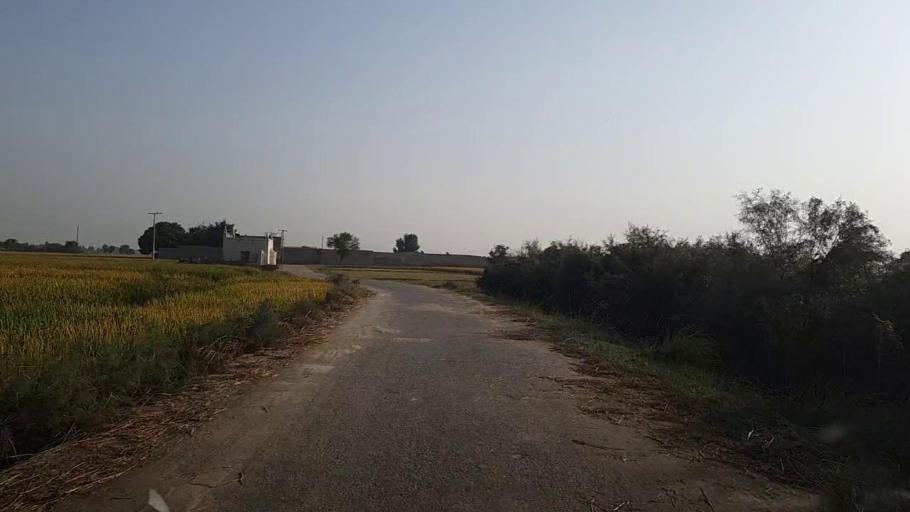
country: PK
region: Sindh
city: Kandhkot
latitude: 28.2527
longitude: 69.1600
